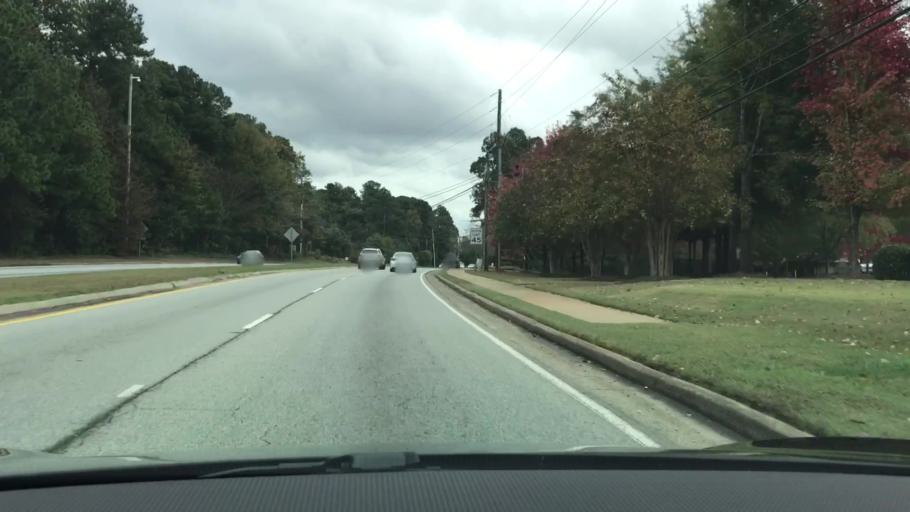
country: US
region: Georgia
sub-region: Gwinnett County
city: Lawrenceville
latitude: 33.9886
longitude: -84.0275
